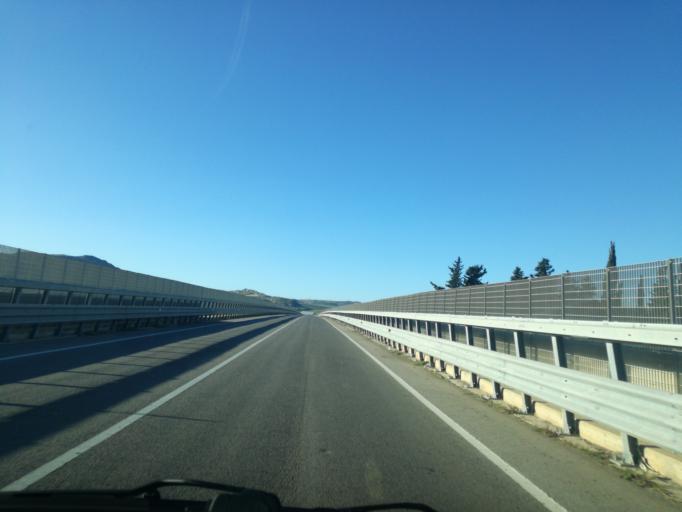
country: IT
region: Sicily
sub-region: Provincia di Caltanissetta
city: Butera
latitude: 37.1371
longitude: 14.1146
